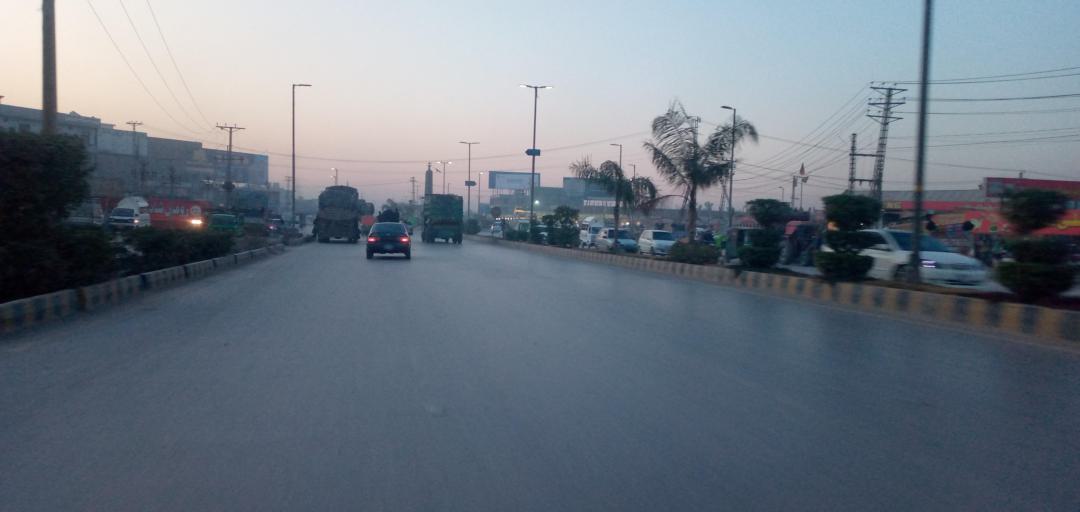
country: PK
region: Khyber Pakhtunkhwa
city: Peshawar
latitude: 34.0313
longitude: 71.6083
